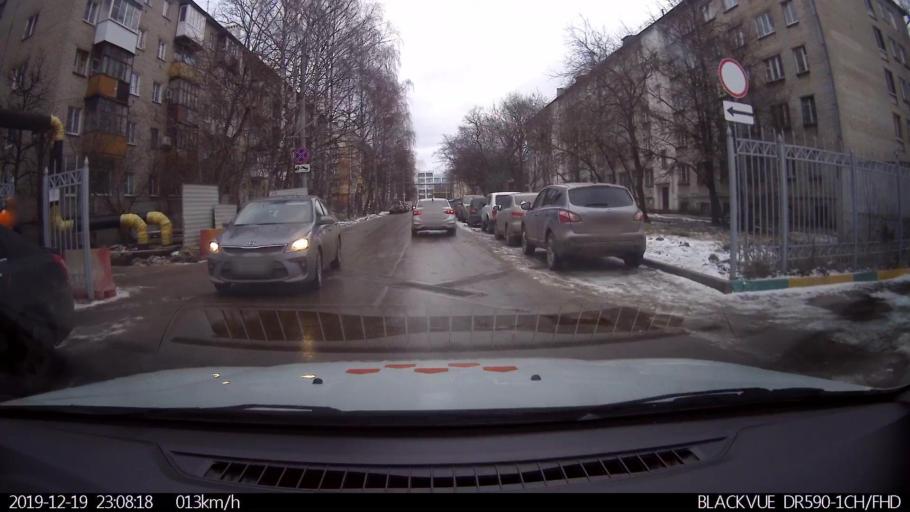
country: RU
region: Nizjnij Novgorod
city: Nizhniy Novgorod
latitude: 56.3005
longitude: 43.9783
